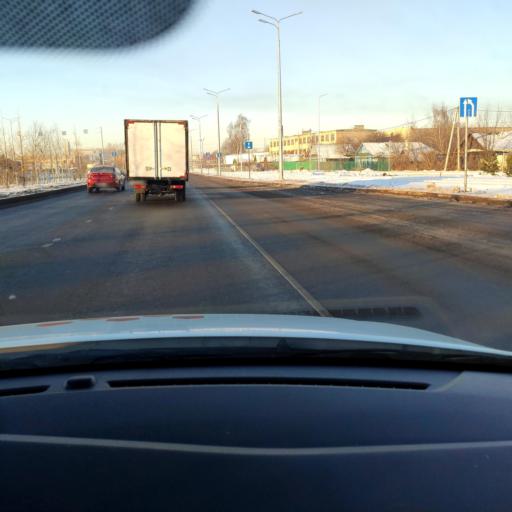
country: RU
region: Tatarstan
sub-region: Gorod Kazan'
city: Kazan
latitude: 55.7307
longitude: 49.1407
